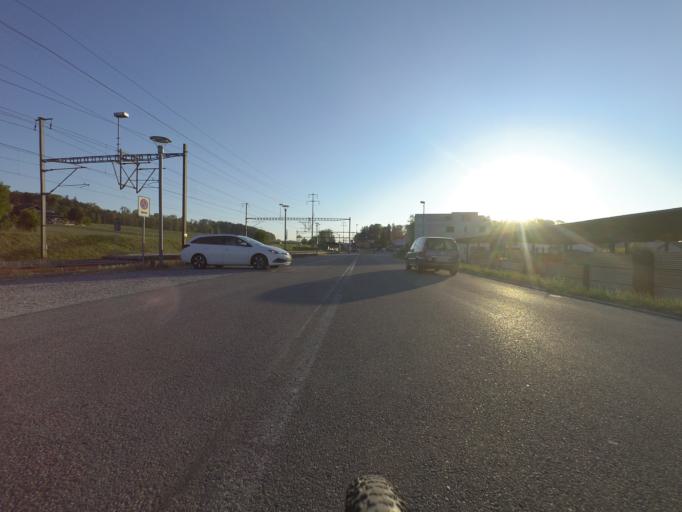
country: CH
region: Zurich
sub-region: Bezirk Winterthur
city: Sulz
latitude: 47.5358
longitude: 8.7910
